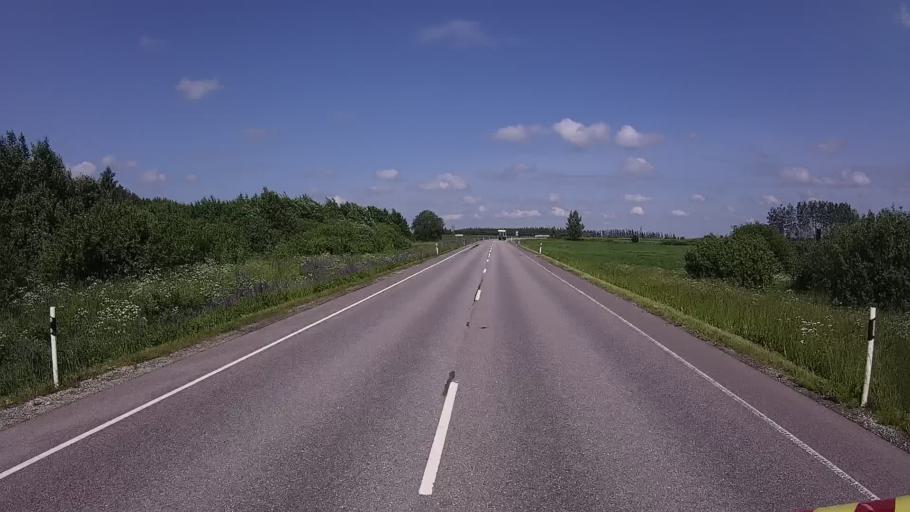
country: EE
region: Tartu
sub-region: UElenurme vald
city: Ulenurme
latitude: 58.2219
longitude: 26.7891
